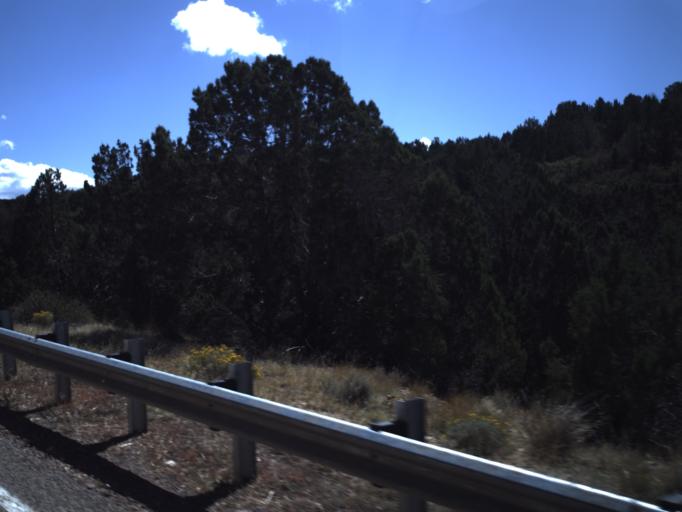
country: US
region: Utah
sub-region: Washington County
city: Enterprise
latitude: 37.5407
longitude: -113.6611
